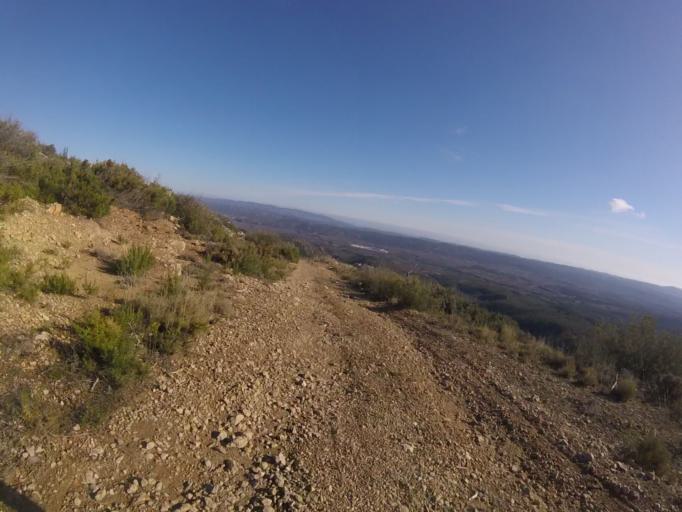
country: ES
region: Valencia
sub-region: Provincia de Castello
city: Sarratella
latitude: 40.2994
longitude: 0.0434
